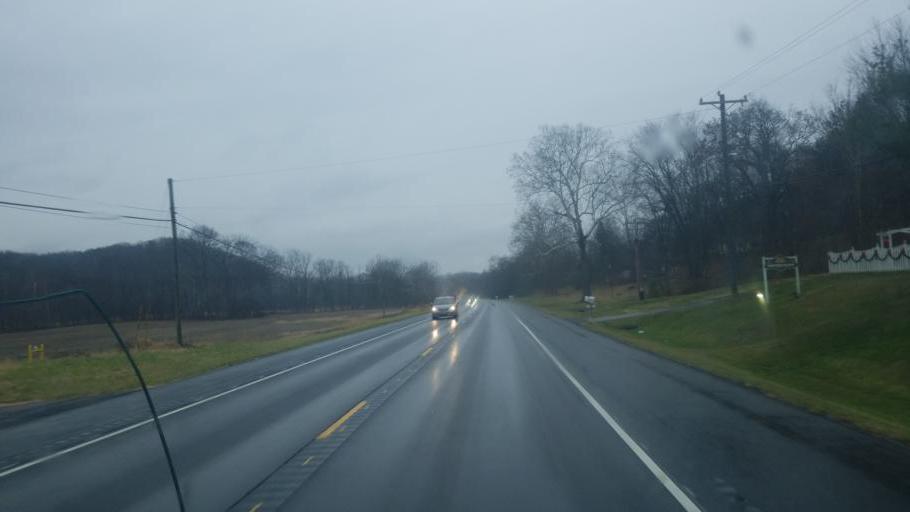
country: US
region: Indiana
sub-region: Brown County
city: Nashville
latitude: 39.1898
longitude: -86.1772
